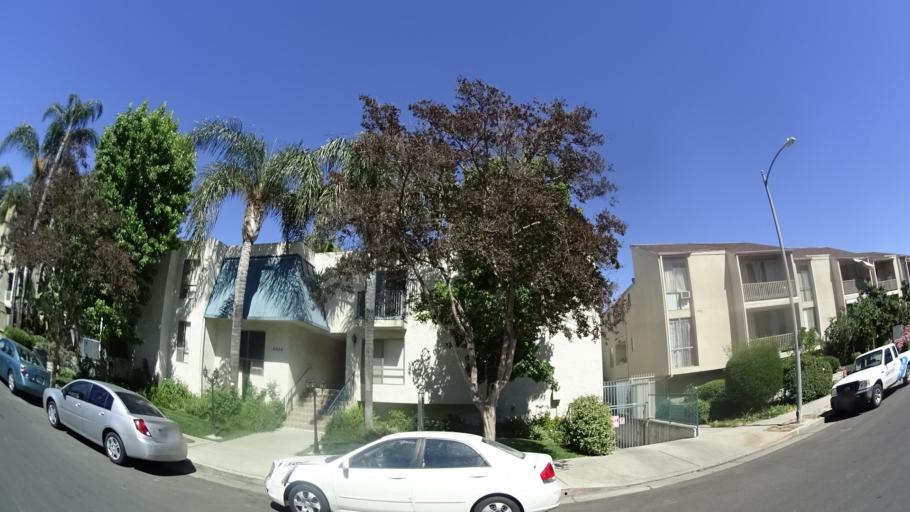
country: US
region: California
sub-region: Los Angeles County
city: Sherman Oaks
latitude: 34.1551
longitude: -118.4542
